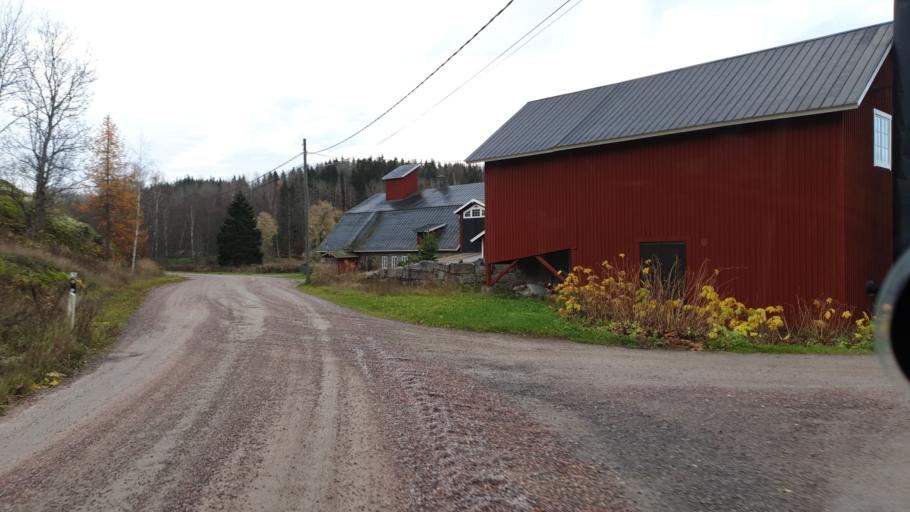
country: FI
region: Uusimaa
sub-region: Helsinki
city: Siuntio
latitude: 60.1439
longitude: 24.2609
